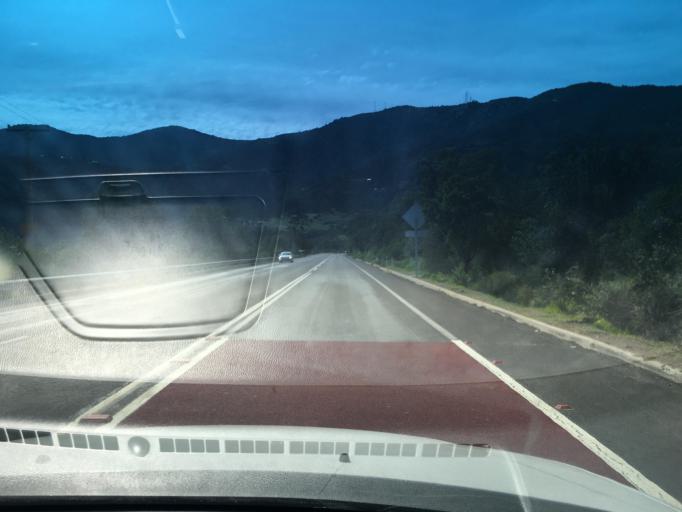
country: CL
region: Valparaiso
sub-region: Provincia de San Felipe
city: Llaillay
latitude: -33.0628
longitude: -71.0309
